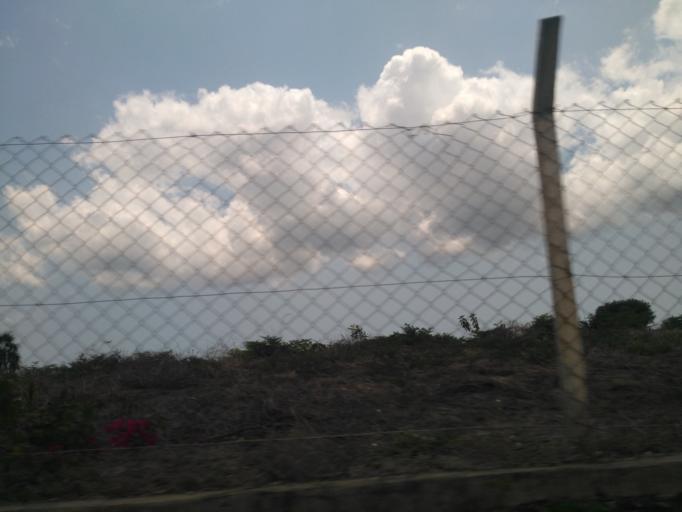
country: TZ
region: Dar es Salaam
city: Dar es Salaam
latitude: -6.8552
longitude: 39.3608
